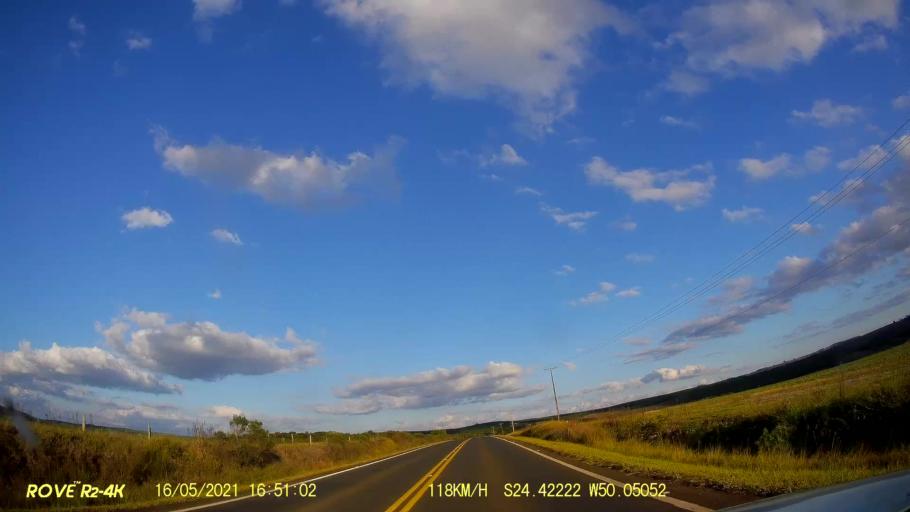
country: BR
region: Parana
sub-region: Pirai Do Sul
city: Pirai do Sul
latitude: -24.4222
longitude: -50.0509
